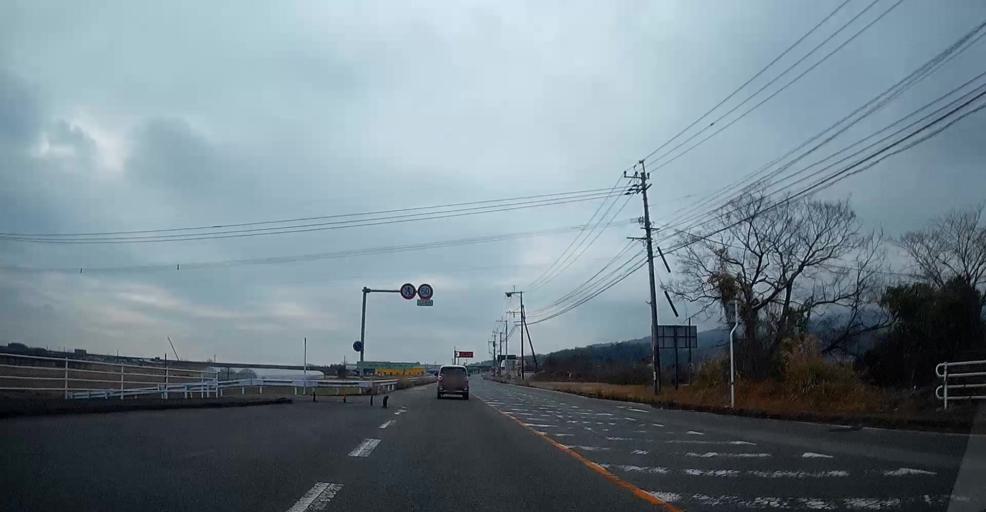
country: JP
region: Kumamoto
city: Matsubase
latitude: 32.6447
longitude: 130.6561
